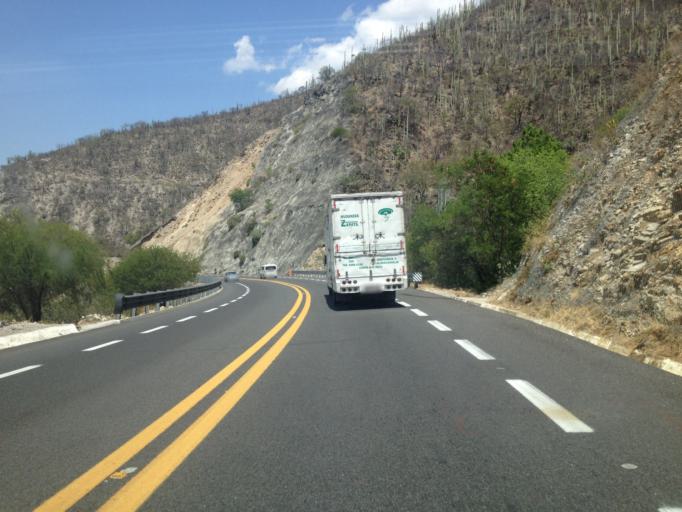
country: MX
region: Puebla
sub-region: San Jose Miahuatlan
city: San Pedro Tetitlan
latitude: 18.1542
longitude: -97.2741
